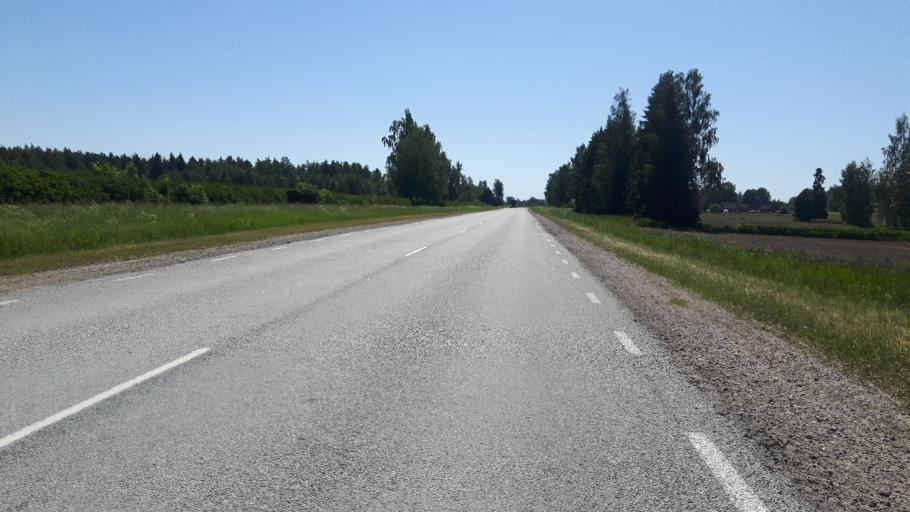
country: EE
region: Paernumaa
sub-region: Tootsi vald
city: Tootsi
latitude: 58.4595
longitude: 24.7807
